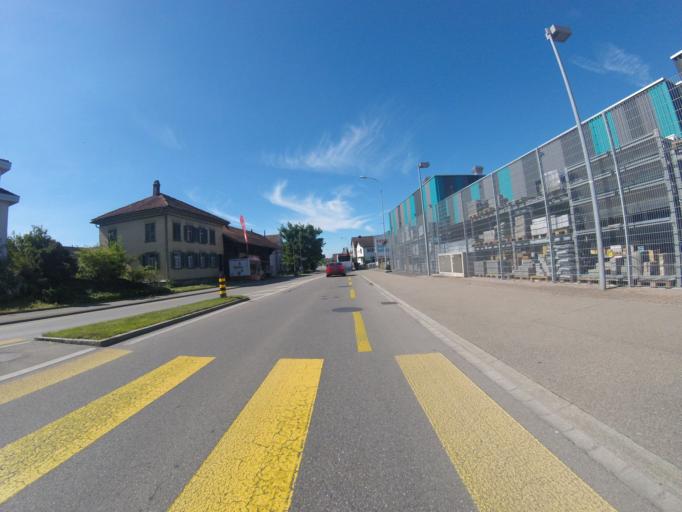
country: CH
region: Saint Gallen
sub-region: Wahlkreis Wil
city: Wil
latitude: 47.4452
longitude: 9.0513
